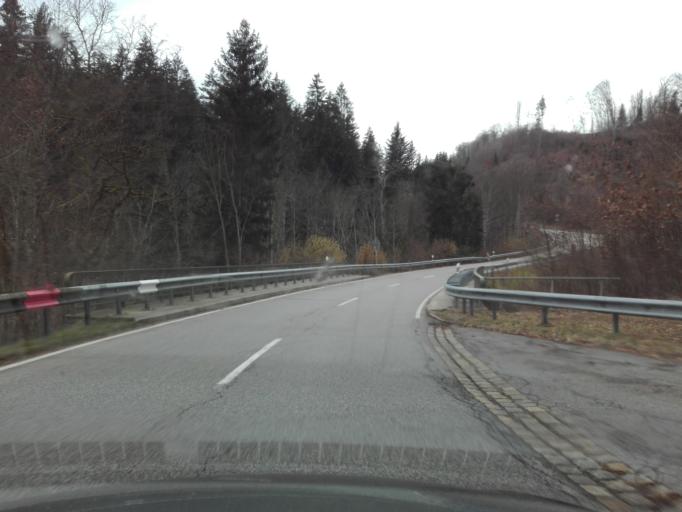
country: DE
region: Bavaria
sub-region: Lower Bavaria
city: Thyrnau
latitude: 48.5939
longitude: 13.5821
